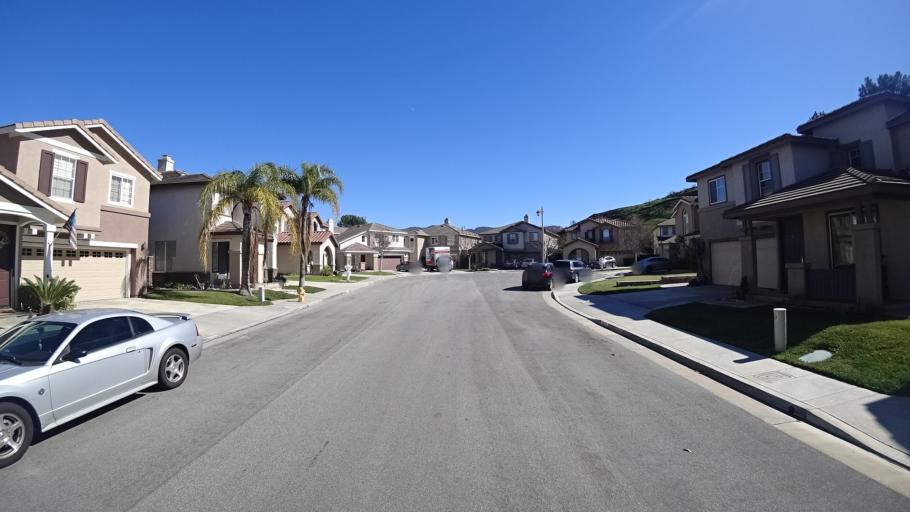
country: US
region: California
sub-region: Orange County
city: Yorba Linda
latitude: 33.8550
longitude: -117.7222
